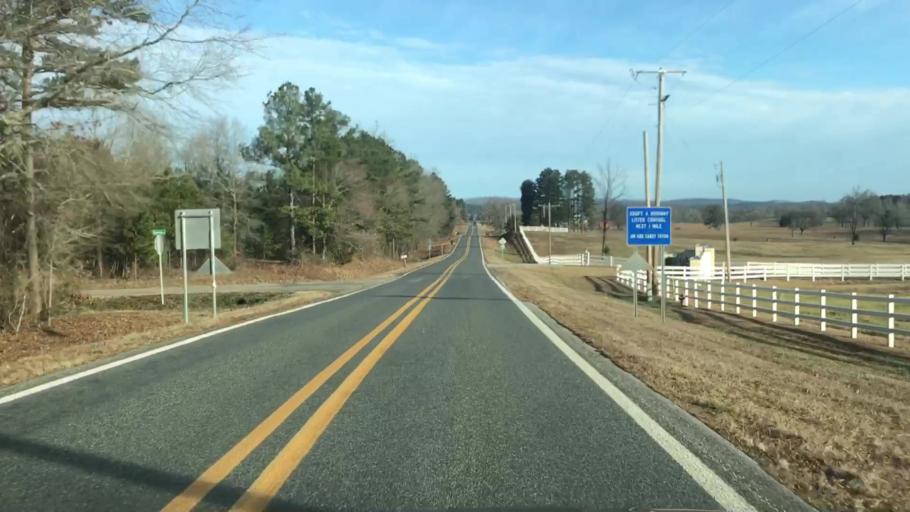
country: US
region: Arkansas
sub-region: Garland County
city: Rockwell
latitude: 34.4953
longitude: -93.2766
